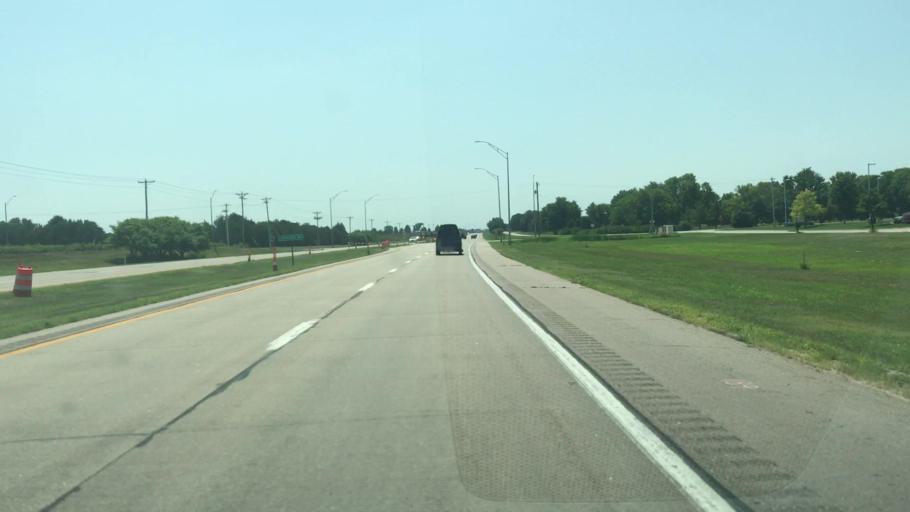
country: US
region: Nebraska
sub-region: Adams County
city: Hastings
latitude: 40.6423
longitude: -98.3820
